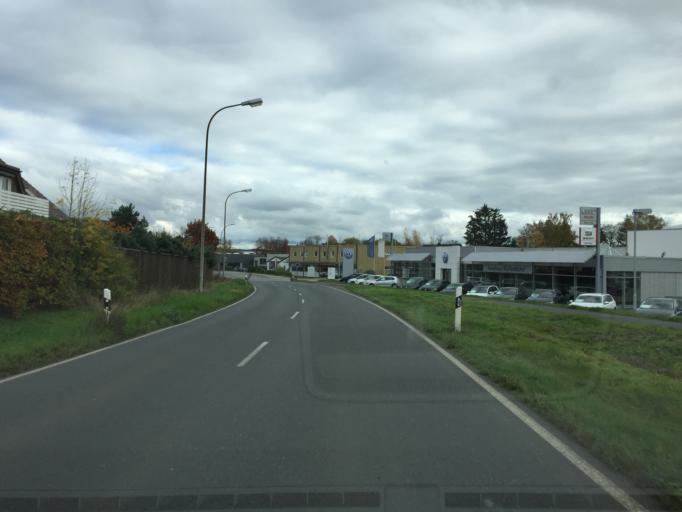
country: DE
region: Lower Saxony
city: Wolfenbuettel
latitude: 52.1646
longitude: 10.5091
